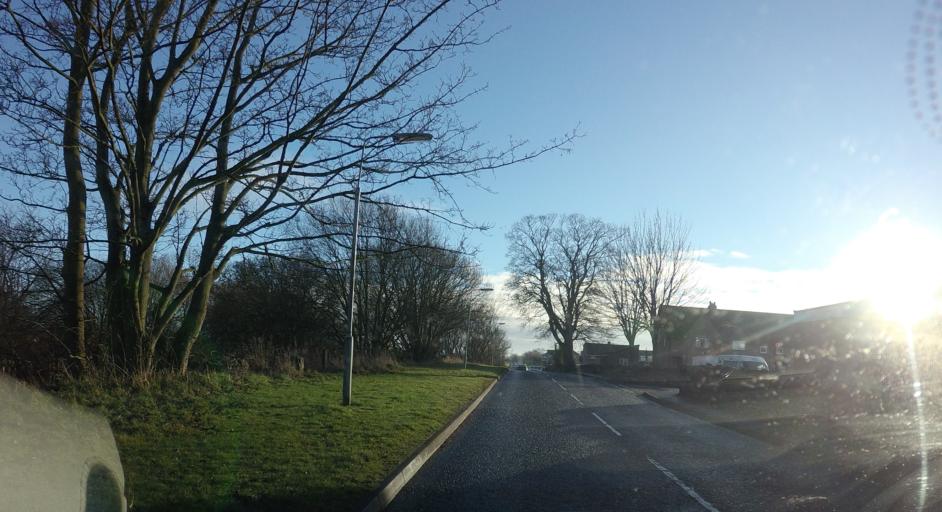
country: GB
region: Scotland
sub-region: Fife
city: Crossford
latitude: 56.0610
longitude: -3.4955
